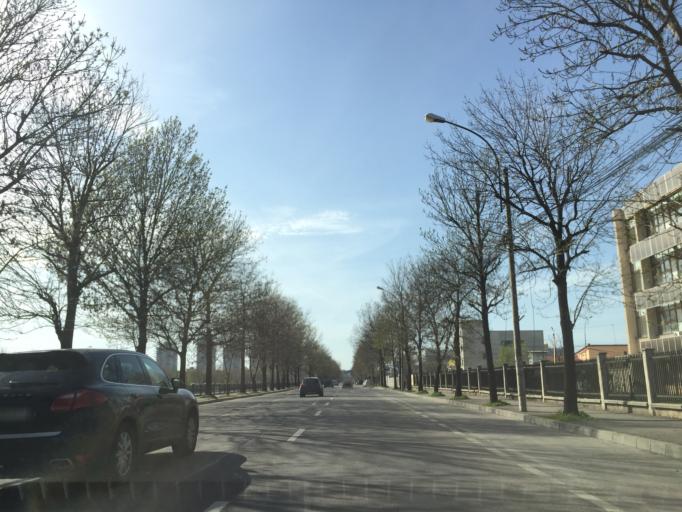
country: RO
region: Ilfov
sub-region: Comuna Popesti-Leordeni
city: Popesti-Leordeni
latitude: 44.4053
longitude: 26.1373
